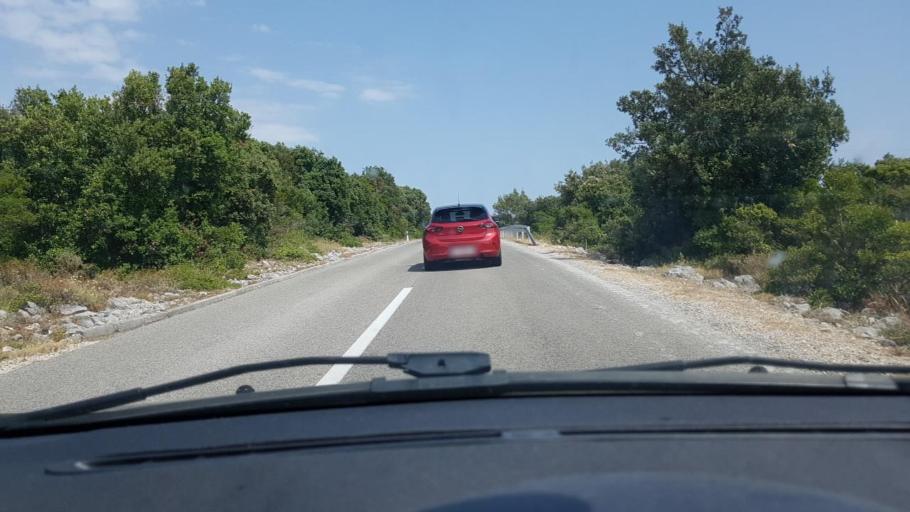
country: HR
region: Dubrovacko-Neretvanska
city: Smokvica
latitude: 42.9488
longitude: 16.9768
